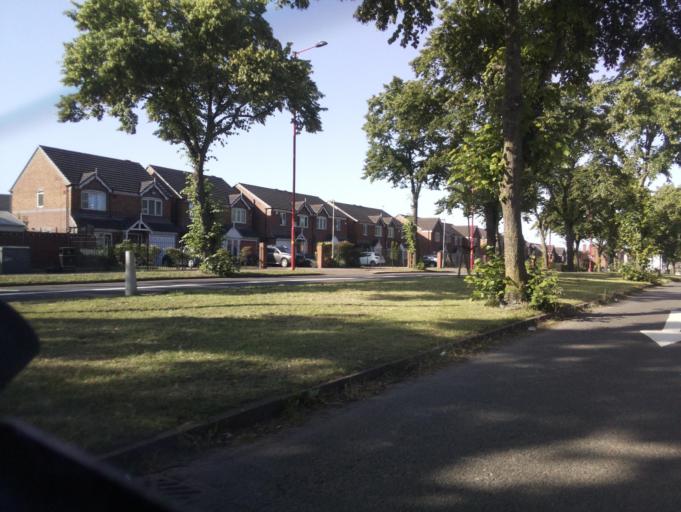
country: GB
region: England
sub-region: City and Borough of Birmingham
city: Sutton Coldfield
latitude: 52.5185
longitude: -1.8156
